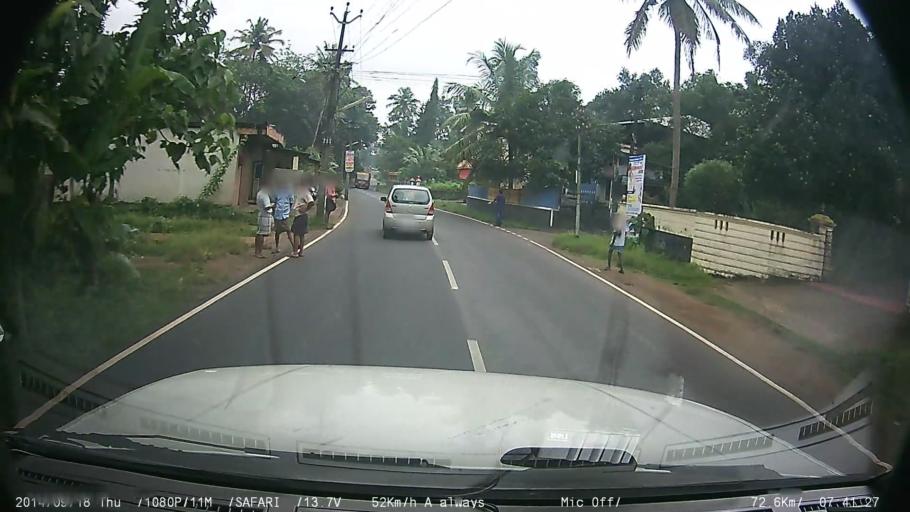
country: IN
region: Kerala
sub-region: Kottayam
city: Changanacheri
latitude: 9.4601
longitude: 76.5776
